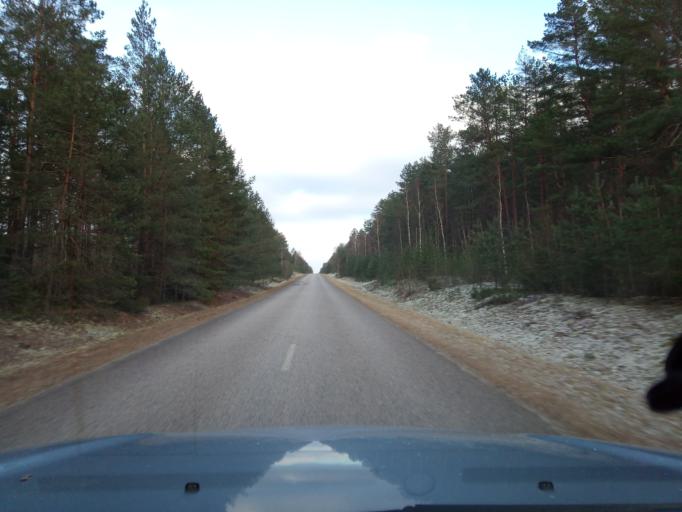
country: LT
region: Alytaus apskritis
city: Varena
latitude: 54.0845
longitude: 24.4051
